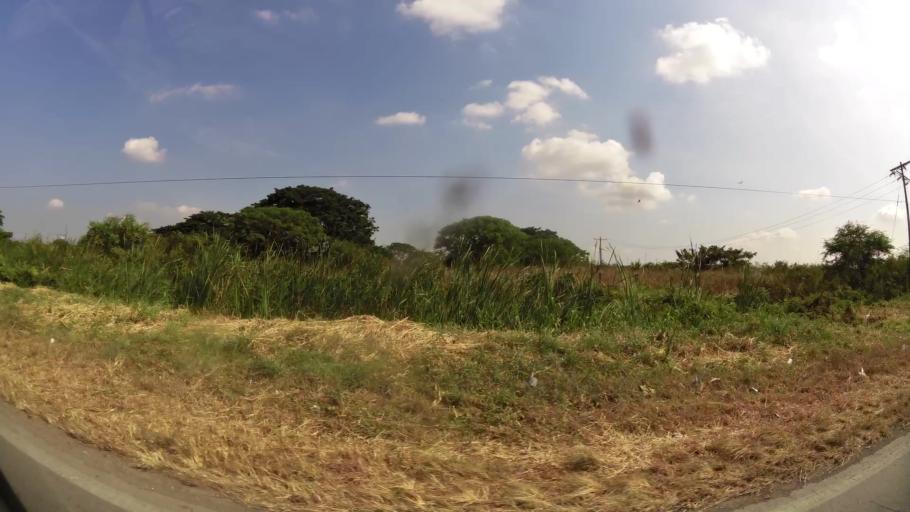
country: EC
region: Guayas
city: Eloy Alfaro
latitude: -2.1837
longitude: -79.8112
